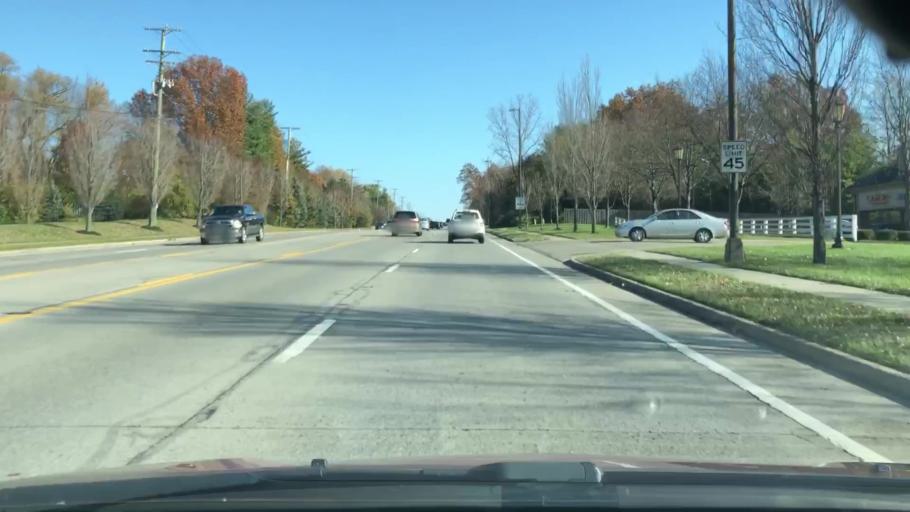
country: US
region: Ohio
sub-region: Franklin County
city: Gahanna
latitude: 40.0561
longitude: -82.8846
